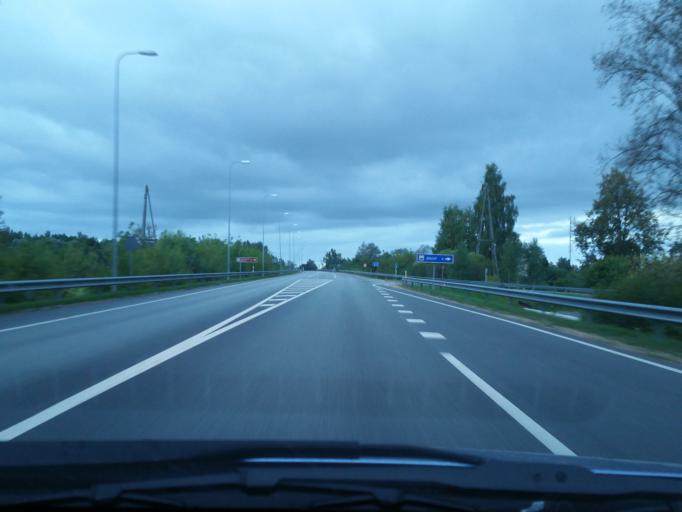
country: LV
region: Adazi
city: Adazi
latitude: 57.1230
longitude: 24.3268
